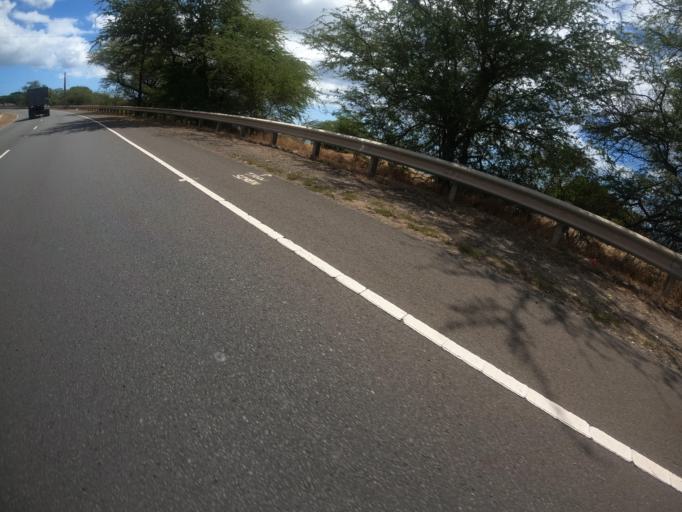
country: US
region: Hawaii
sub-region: Honolulu County
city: Makakilo
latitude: 21.3497
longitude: -158.1297
